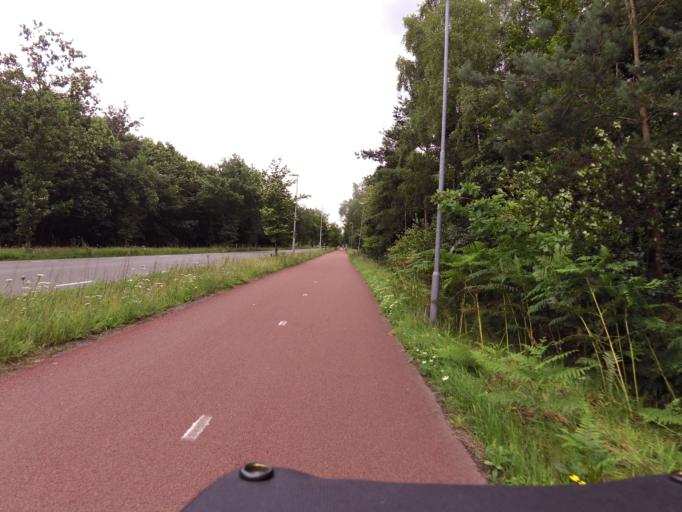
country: NL
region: North Brabant
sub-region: Gemeente Breda
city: Breda
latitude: 51.5859
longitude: 4.6901
